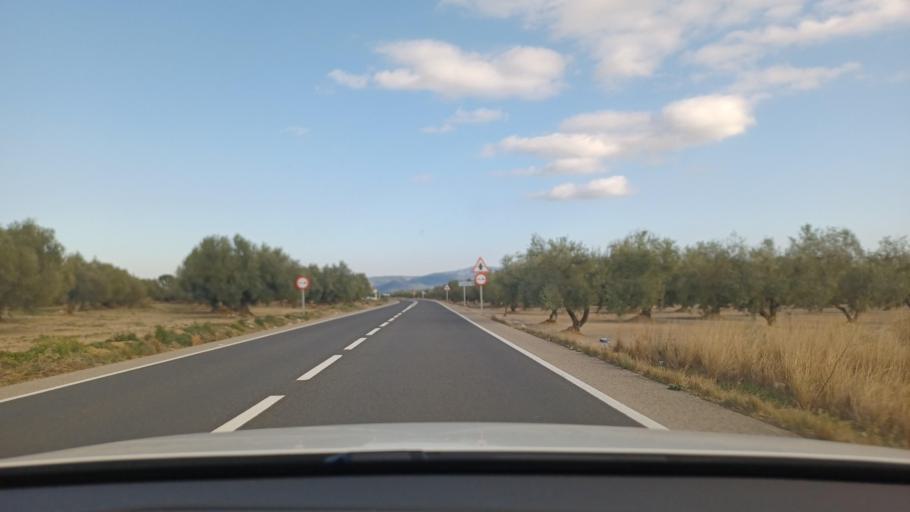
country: ES
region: Catalonia
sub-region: Provincia de Tarragona
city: Ulldecona
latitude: 40.6420
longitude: 0.3707
